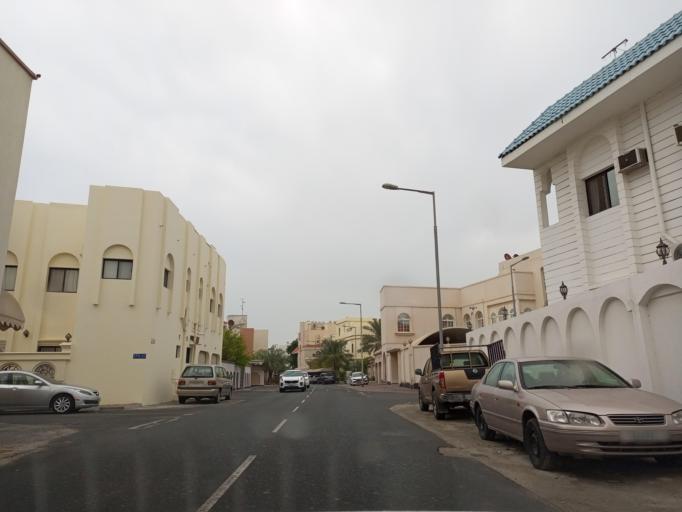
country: BH
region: Muharraq
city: Al Hadd
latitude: 26.2585
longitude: 50.6355
